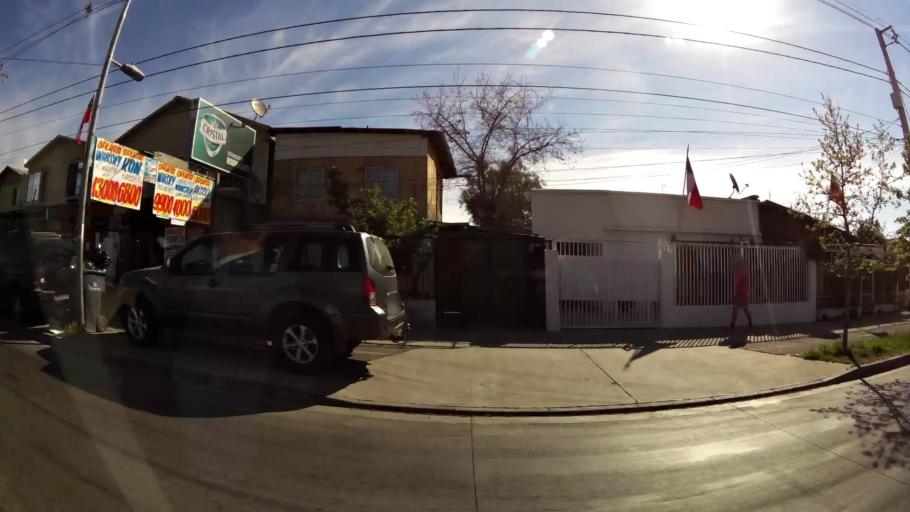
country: CL
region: Santiago Metropolitan
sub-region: Provincia de Santiago
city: La Pintana
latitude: -33.5221
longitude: -70.6233
